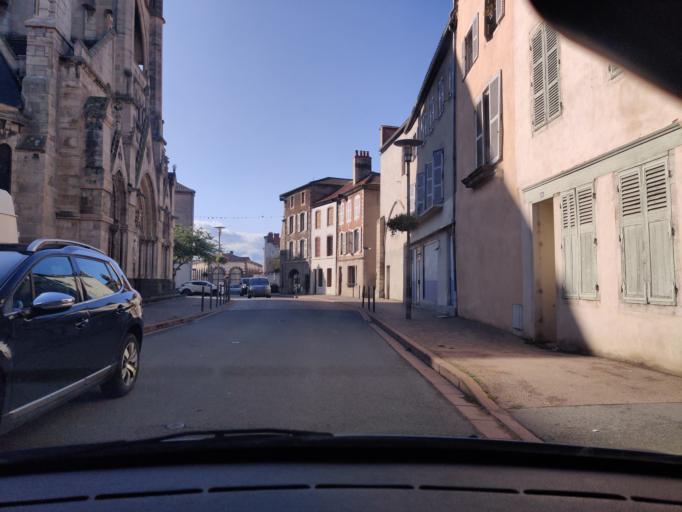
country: FR
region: Auvergne
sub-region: Departement du Puy-de-Dome
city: Aigueperse
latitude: 46.0223
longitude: 3.2020
